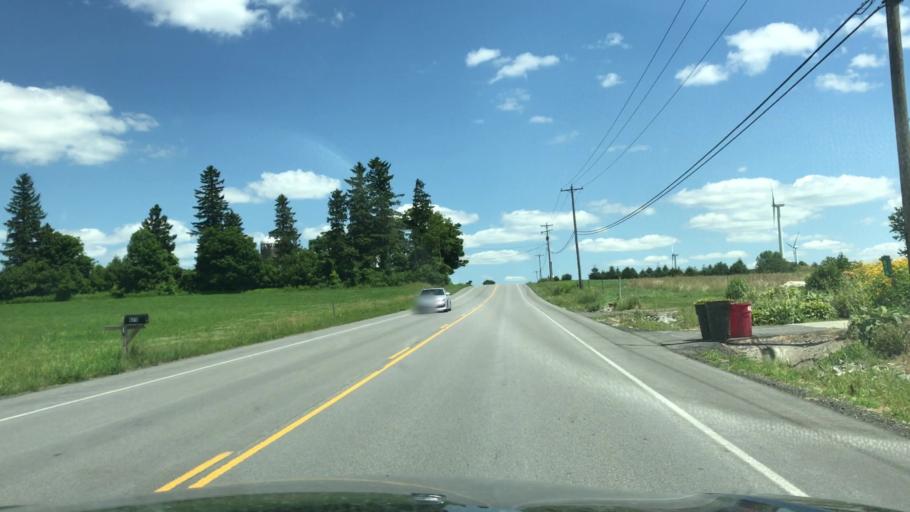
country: US
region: New York
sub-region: Erie County
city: Alden
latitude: 42.7698
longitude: -78.4261
